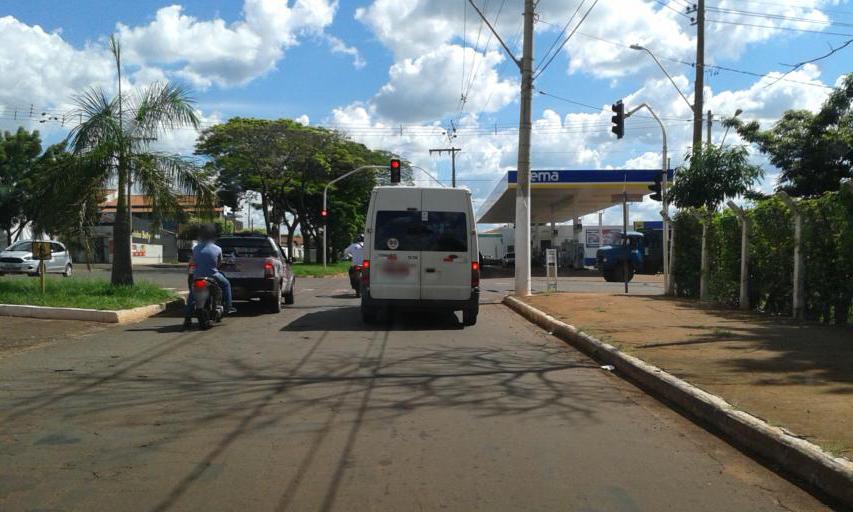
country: BR
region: Minas Gerais
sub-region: Ituiutaba
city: Ituiutaba
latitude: -18.9748
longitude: -49.4835
